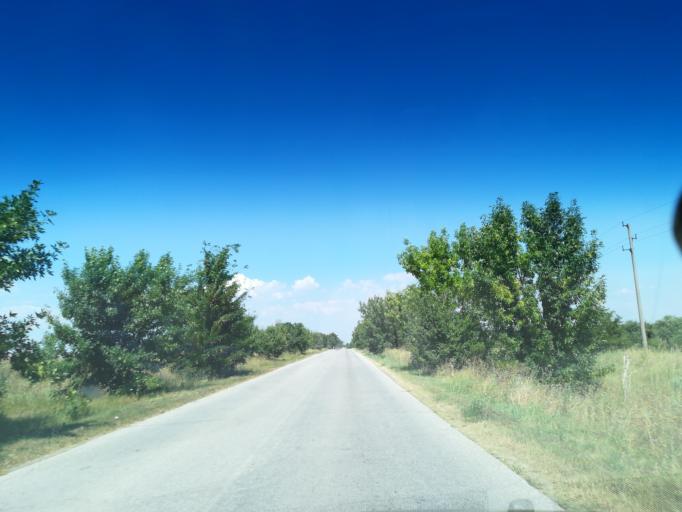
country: BG
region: Plovdiv
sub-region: Obshtina Sadovo
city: Sadovo
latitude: 42.0512
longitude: 25.1471
